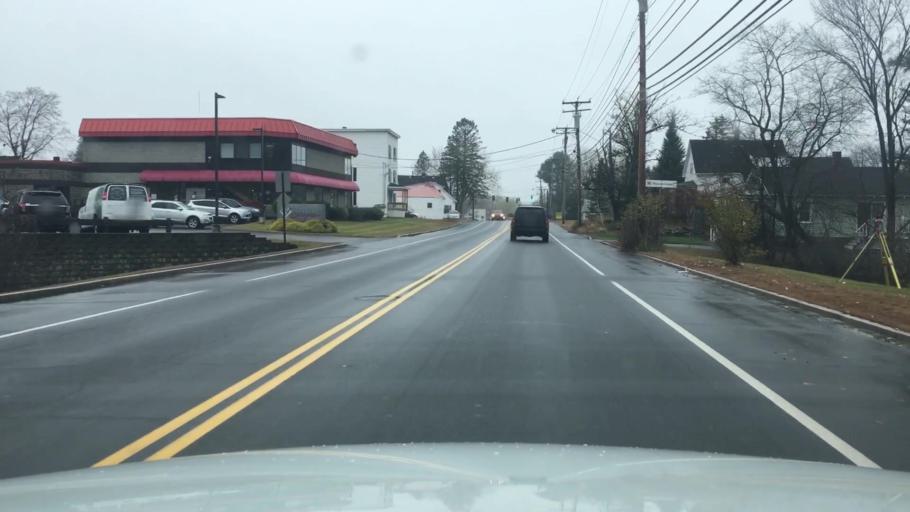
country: US
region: Maine
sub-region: Androscoggin County
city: Sabattus
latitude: 44.1011
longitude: -70.1582
